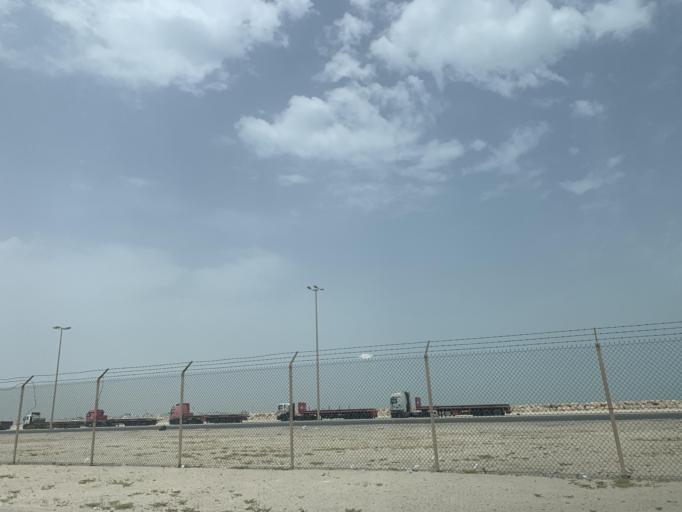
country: BH
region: Muharraq
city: Al Hadd
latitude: 26.2248
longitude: 50.6836
